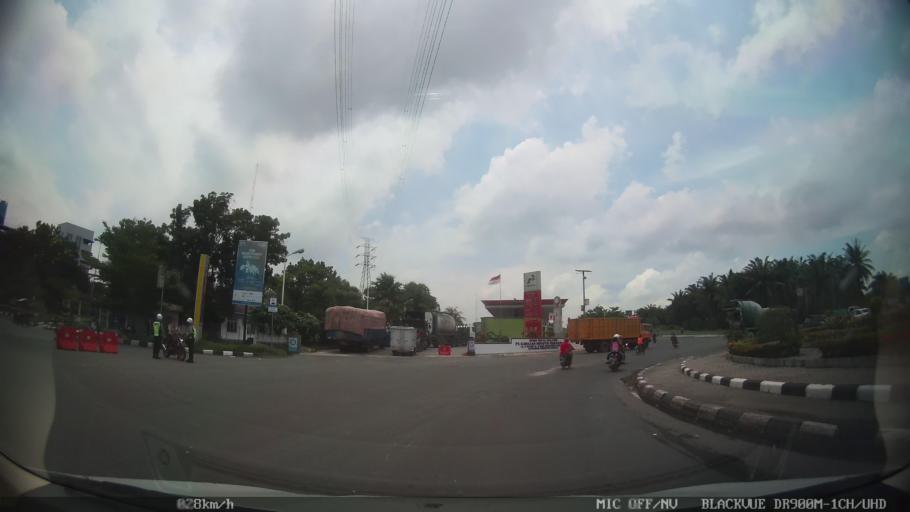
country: ID
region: North Sumatra
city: Labuhan Deli
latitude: 3.6727
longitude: 98.6831
